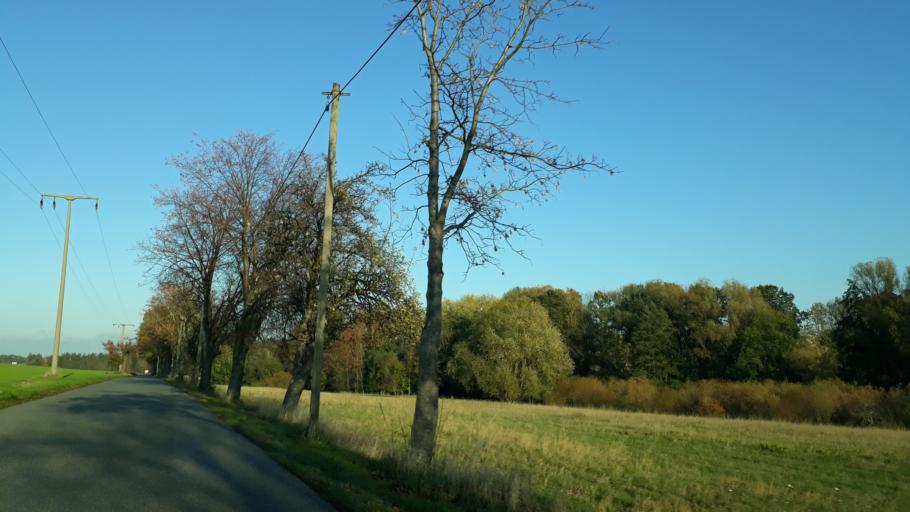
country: DE
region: Saxony
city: Klipphausen
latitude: 51.0637
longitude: 13.4771
